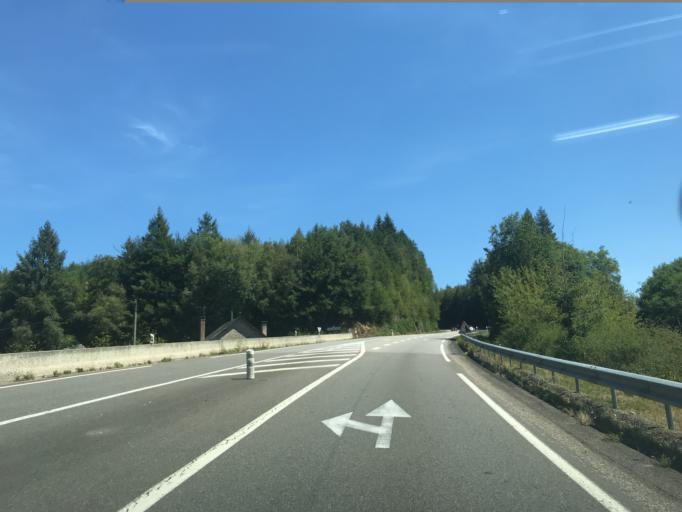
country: FR
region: Limousin
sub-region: Departement de la Correze
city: Naves
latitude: 45.2961
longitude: 1.8098
